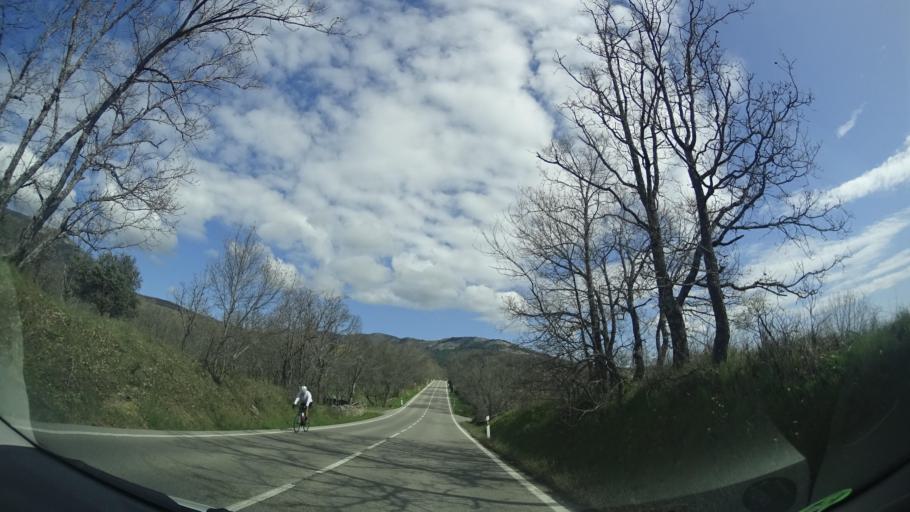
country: ES
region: Madrid
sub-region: Provincia de Madrid
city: Miraflores de la Sierra
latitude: 40.7963
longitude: -3.7749
